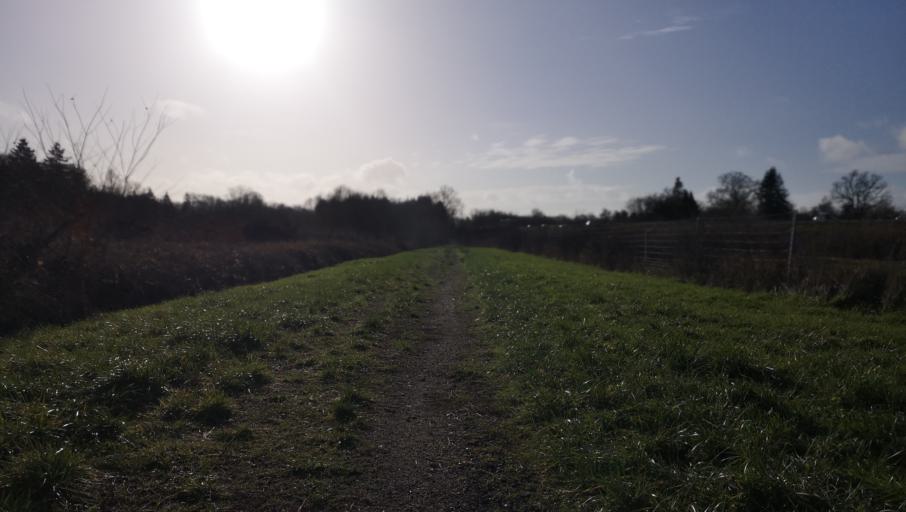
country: FR
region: Centre
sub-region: Departement du Loiret
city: Saint-Pryve-Saint-Mesmin
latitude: 47.8749
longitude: 1.8633
